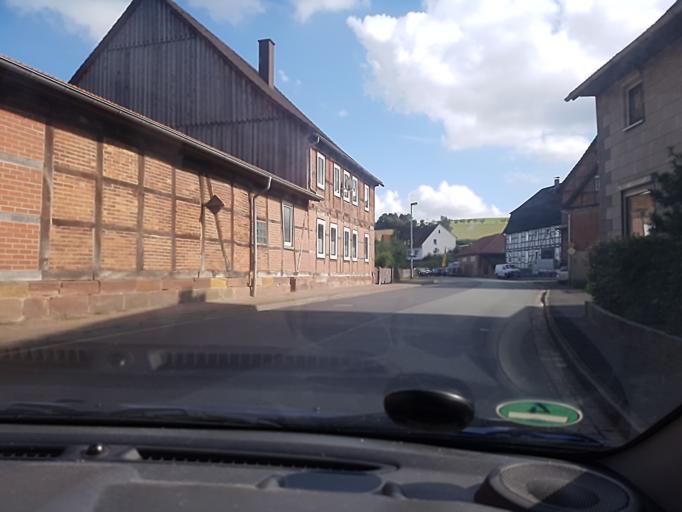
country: DE
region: Lower Saxony
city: Uslar
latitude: 51.6693
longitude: 9.5999
